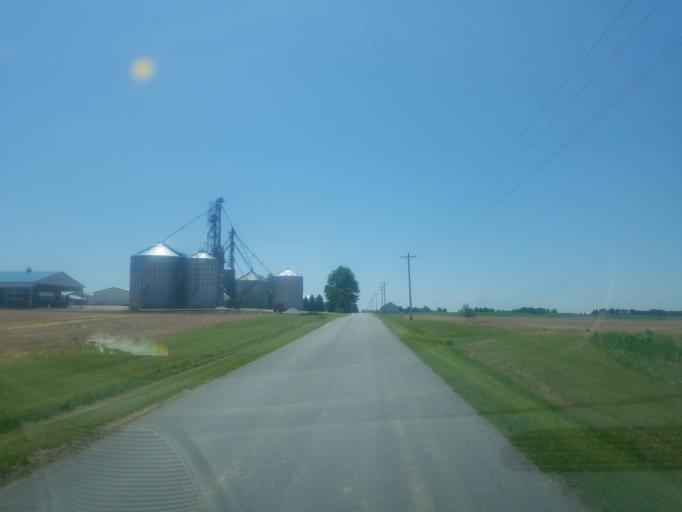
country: US
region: Ohio
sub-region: Huron County
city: New London
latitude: 41.1046
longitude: -82.4626
